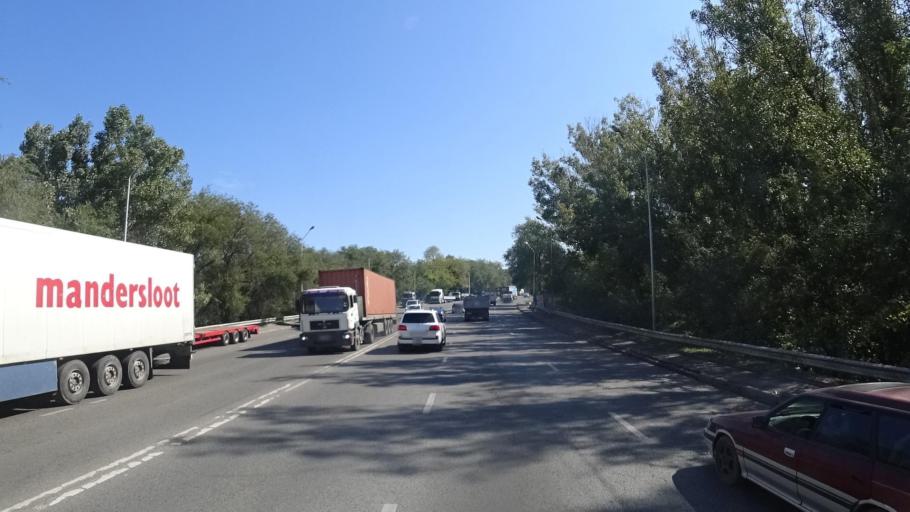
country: KZ
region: Almaty Oblysy
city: Pervomayskiy
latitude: 43.3548
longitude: 76.9443
